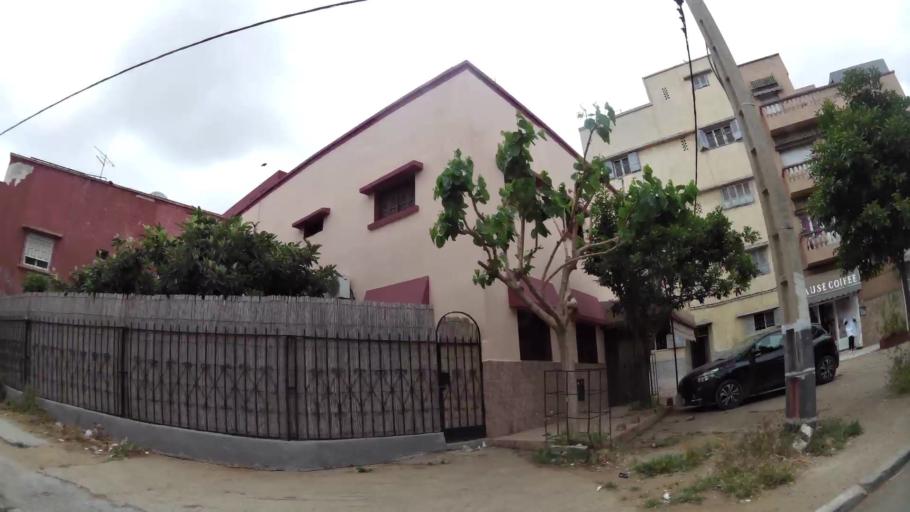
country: MA
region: Rabat-Sale-Zemmour-Zaer
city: Sale
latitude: 34.0416
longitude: -6.8055
